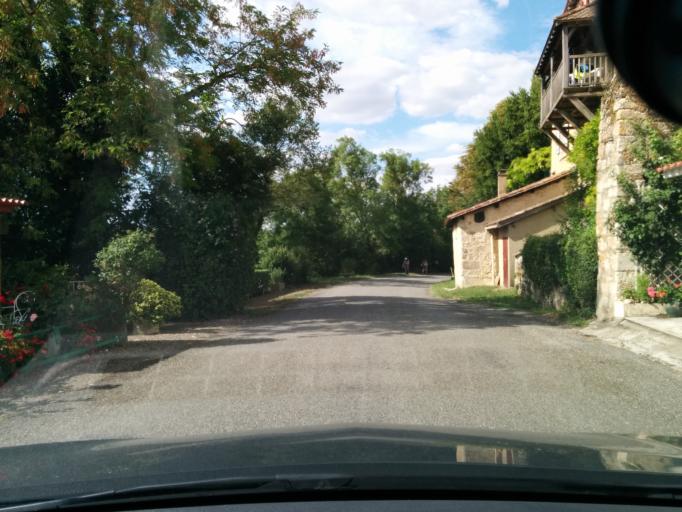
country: FR
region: Midi-Pyrenees
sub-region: Departement du Gers
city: Aubiet
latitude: 43.5757
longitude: 0.7224
